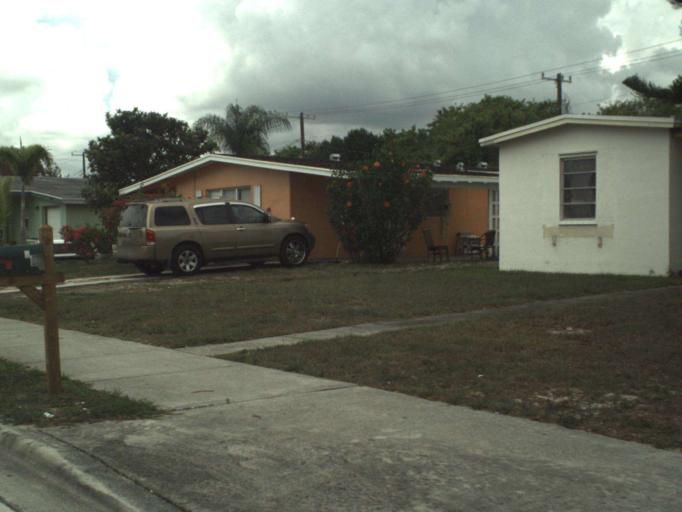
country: US
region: Florida
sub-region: Saint Lucie County
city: River Park
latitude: 27.3165
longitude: -80.3497
